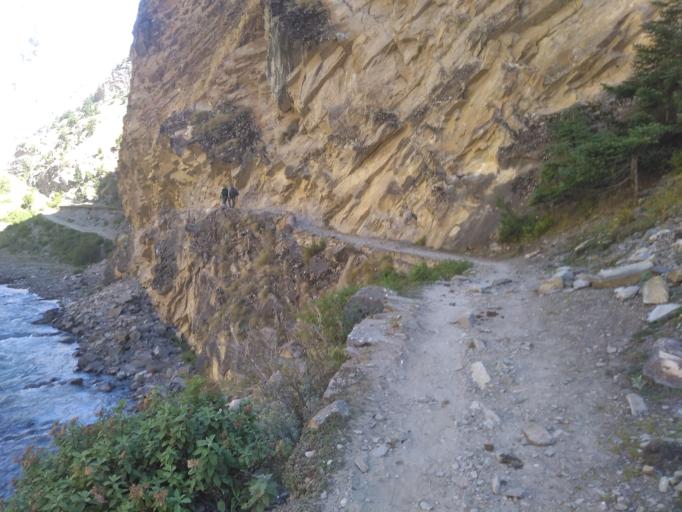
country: NP
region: Western Region
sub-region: Dhawalagiri Zone
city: Jomsom
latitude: 28.9678
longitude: 83.0797
